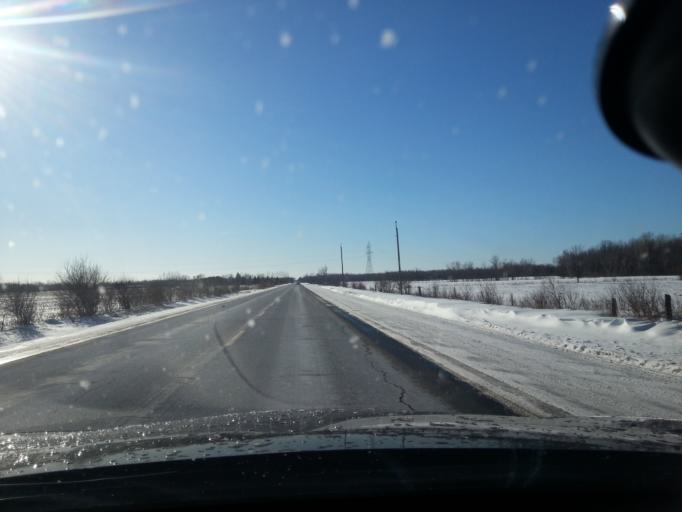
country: CA
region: Ontario
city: Ottawa
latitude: 45.3291
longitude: -75.4510
